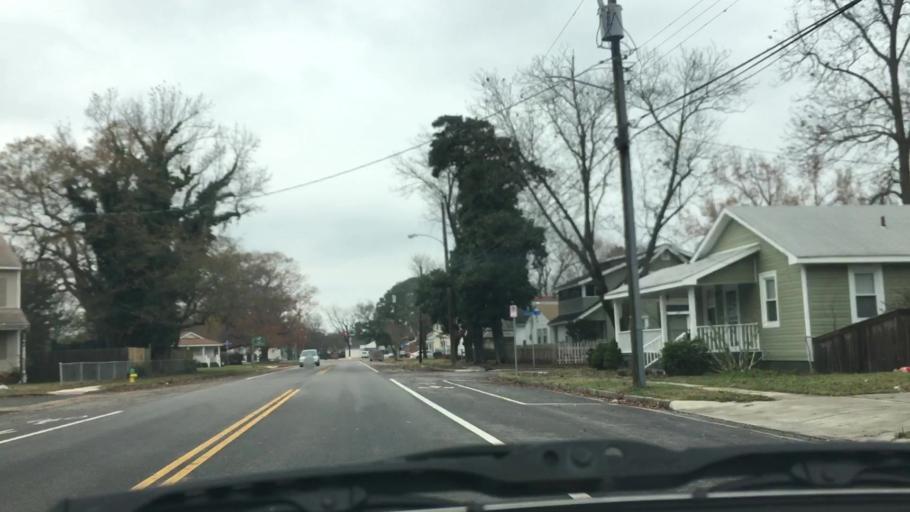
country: US
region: Virginia
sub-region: City of Norfolk
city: Norfolk
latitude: 36.8780
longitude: -76.2471
